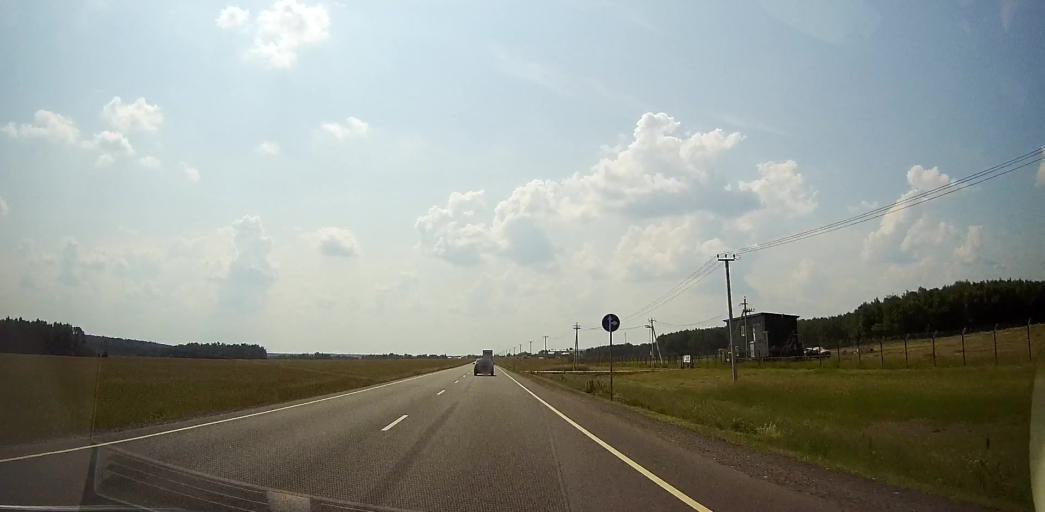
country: RU
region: Moskovskaya
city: Meshcherino
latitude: 55.1557
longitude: 38.3072
